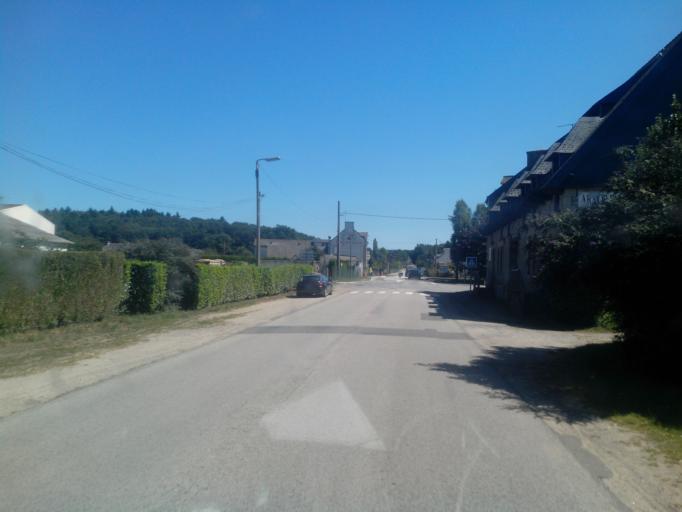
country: FR
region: Brittany
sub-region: Departement du Morbihan
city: Guillac
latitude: 47.8651
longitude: -2.4400
